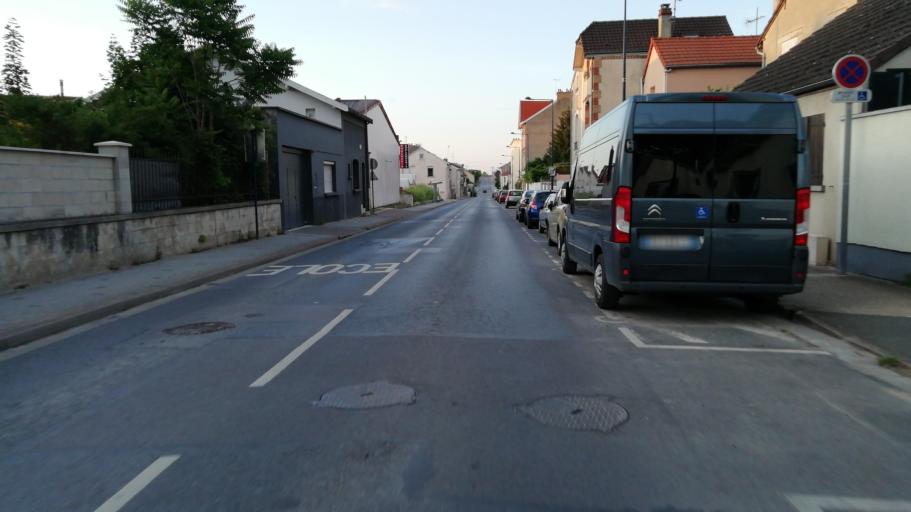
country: FR
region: Champagne-Ardenne
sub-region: Departement de la Marne
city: Betheny
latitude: 49.2699
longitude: 4.0490
